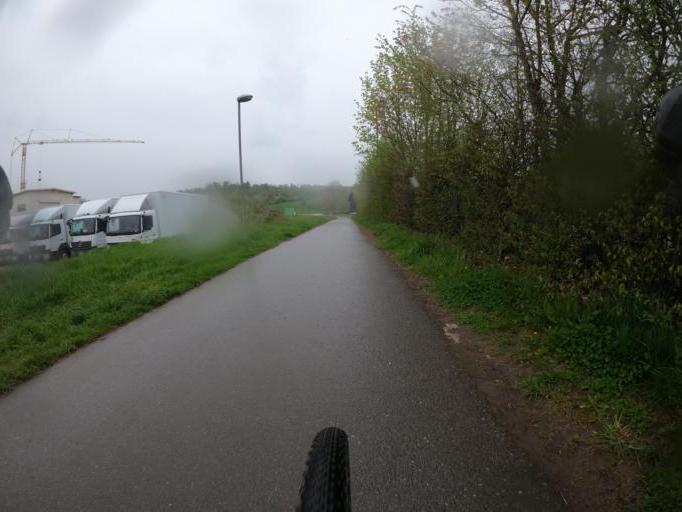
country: DE
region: Baden-Wuerttemberg
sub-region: Regierungsbezirk Stuttgart
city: Vaihingen an der Enz
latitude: 48.9240
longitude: 8.9744
